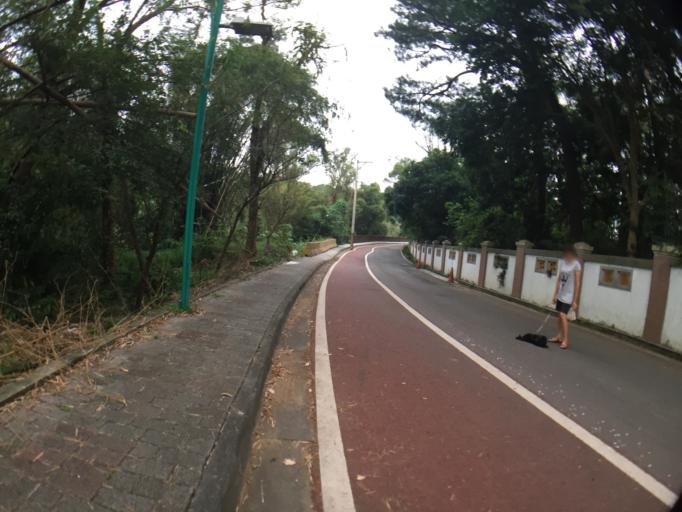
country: TW
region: Taiwan
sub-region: Hsinchu
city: Hsinchu
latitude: 24.7725
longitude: 120.9747
